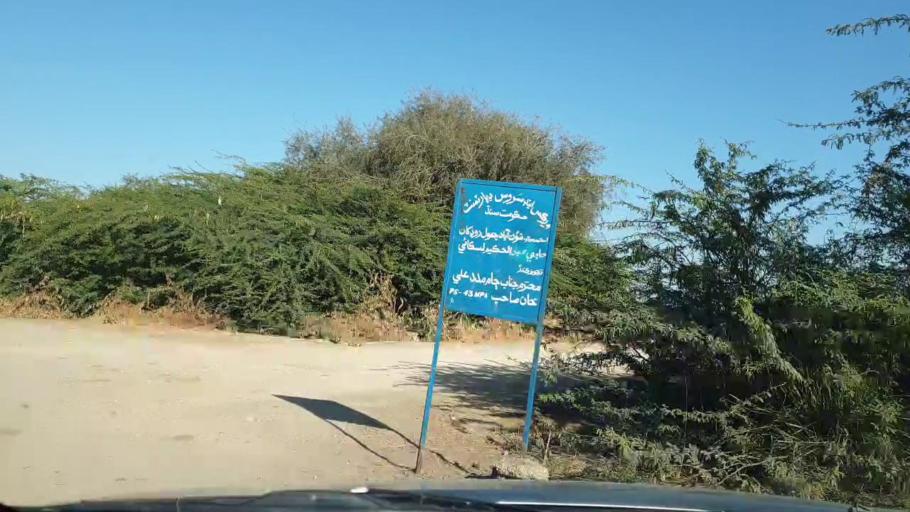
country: PK
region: Sindh
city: Jhol
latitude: 25.8515
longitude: 68.9530
